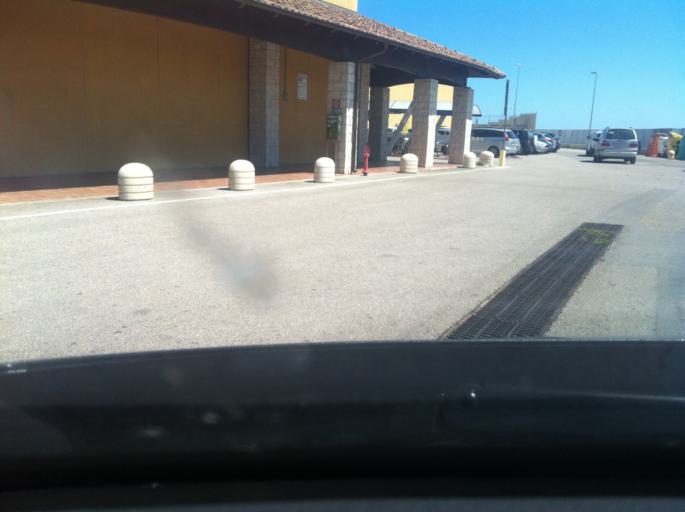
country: IT
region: Apulia
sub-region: Provincia di Foggia
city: Manfredonia
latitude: 41.6443
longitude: 15.9374
